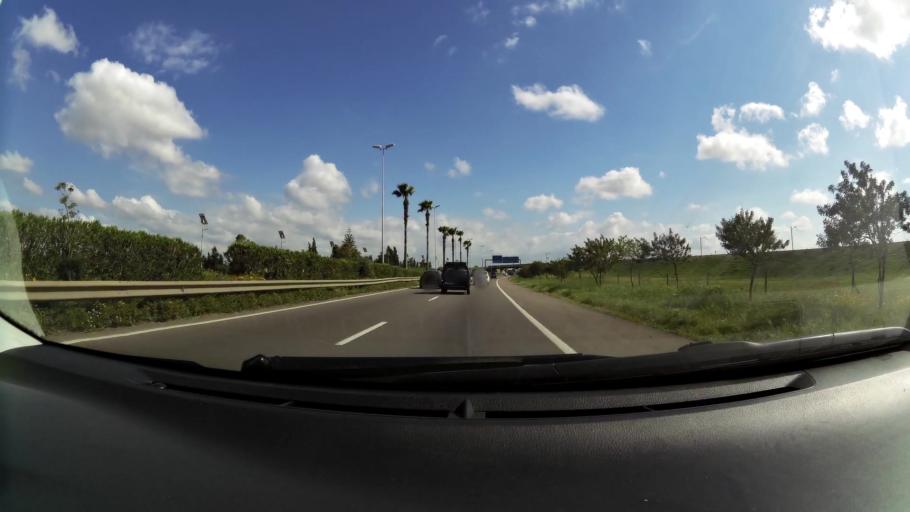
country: MA
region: Chaouia-Ouardigha
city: Nouaseur
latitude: 33.3999
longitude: -7.6214
